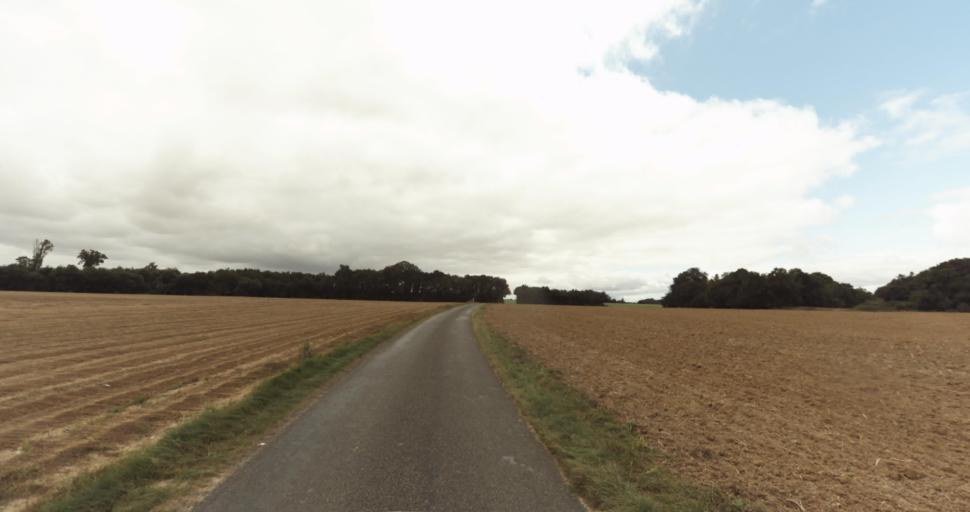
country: FR
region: Haute-Normandie
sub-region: Departement de l'Eure
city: La Madeleine-de-Nonancourt
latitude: 48.9005
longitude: 1.2032
